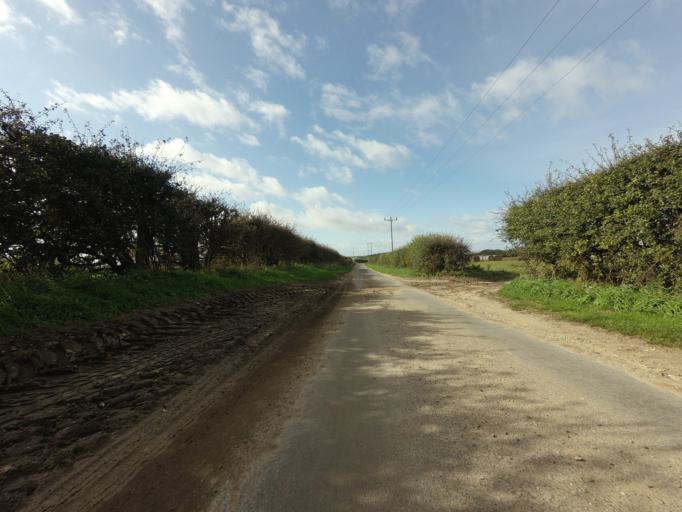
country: GB
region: England
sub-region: Norfolk
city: Hunstanton
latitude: 52.9355
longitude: 0.6432
